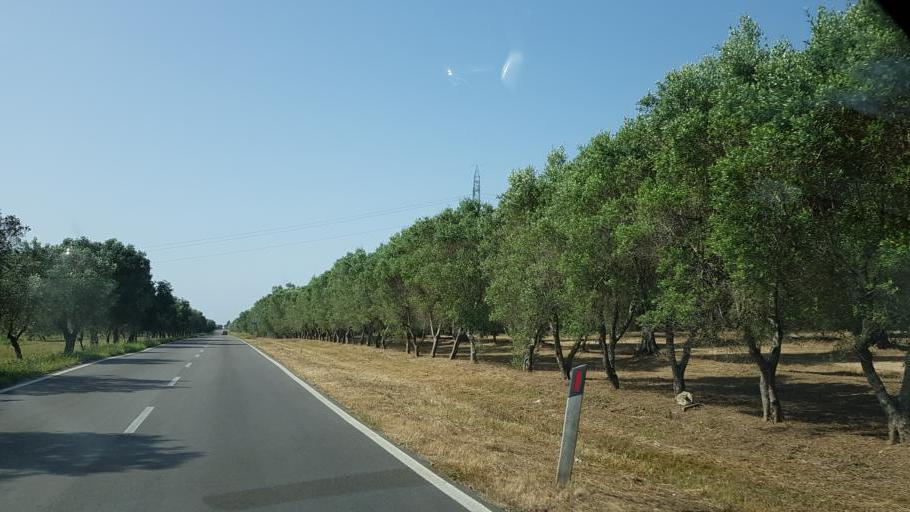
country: IT
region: Apulia
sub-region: Provincia di Brindisi
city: San Pancrazio Salentino
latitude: 40.3624
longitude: 17.8420
